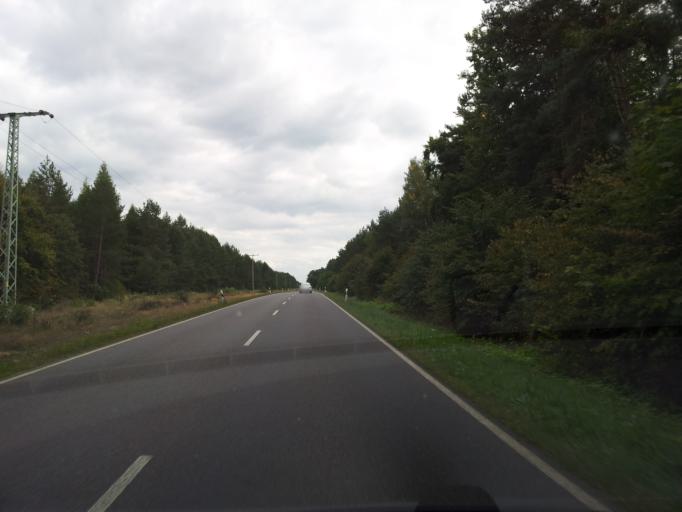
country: DE
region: Brandenburg
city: Guteborn
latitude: 51.4182
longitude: 13.9362
